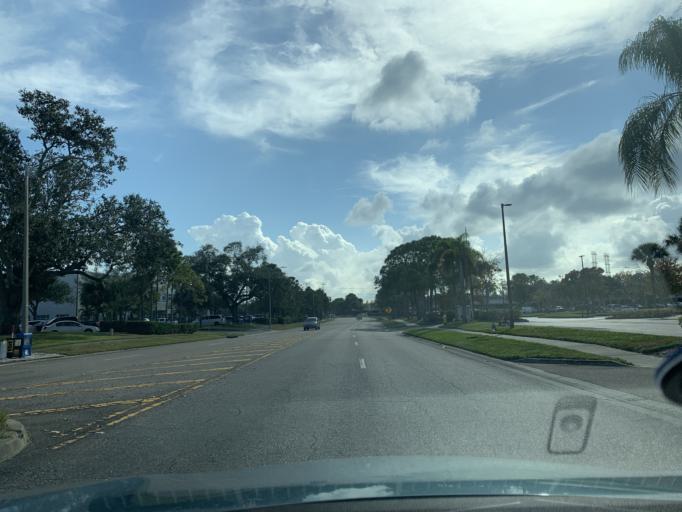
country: US
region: Florida
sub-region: Pinellas County
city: South Highpoint
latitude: 27.9005
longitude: -82.7127
